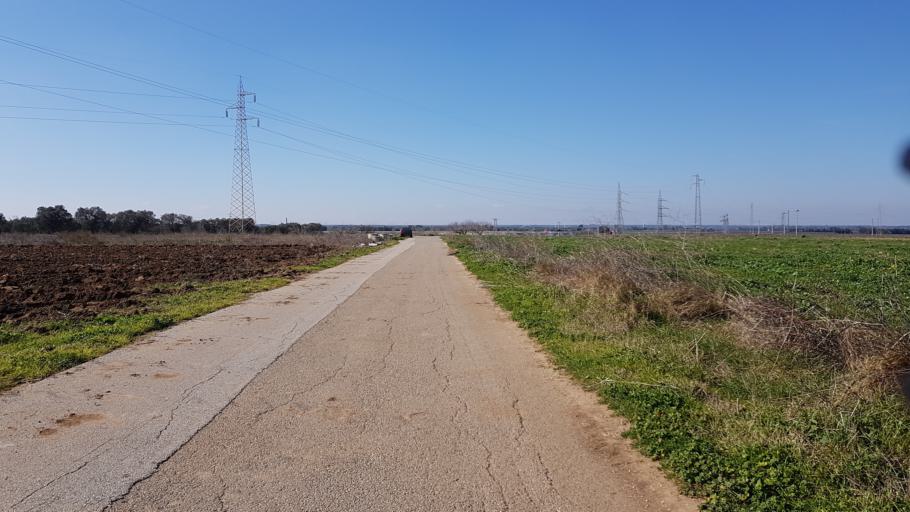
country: IT
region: Apulia
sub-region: Provincia di Brindisi
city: Mesagne
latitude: 40.6209
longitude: 17.8240
